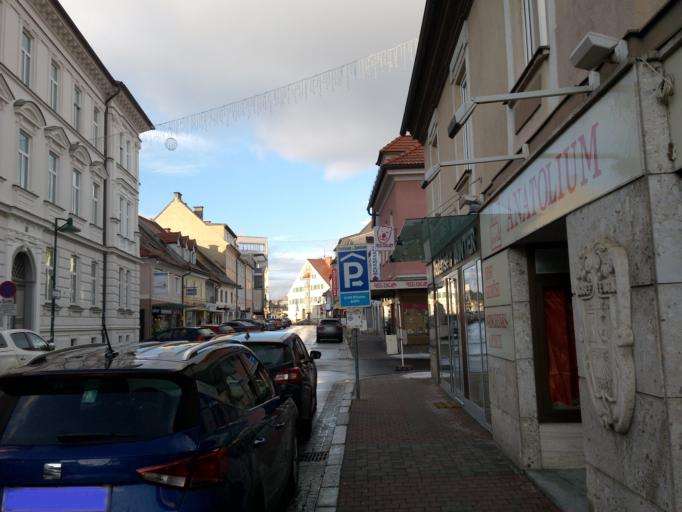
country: AT
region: Styria
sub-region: Politischer Bezirk Murtal
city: Knittelfeld
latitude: 47.2152
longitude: 14.8291
